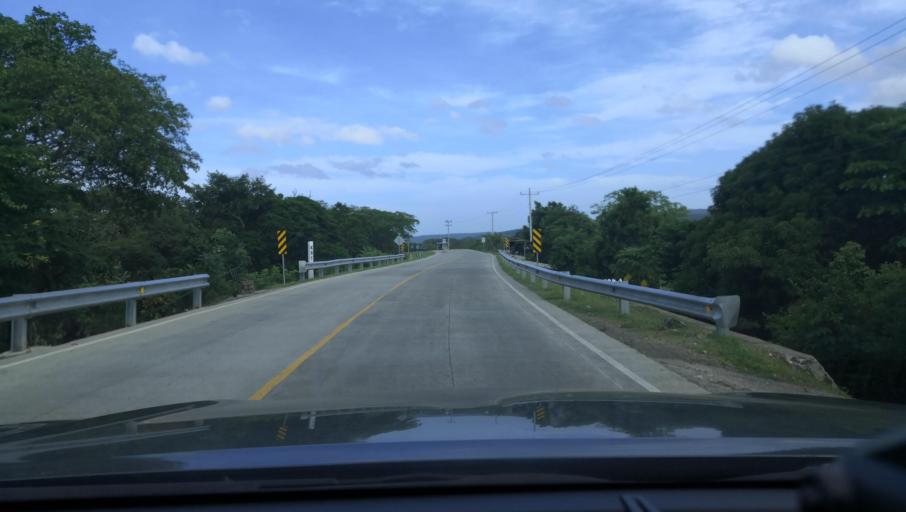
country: NI
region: Boaco
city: San Lorenzo
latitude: 12.1889
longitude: -85.7107
